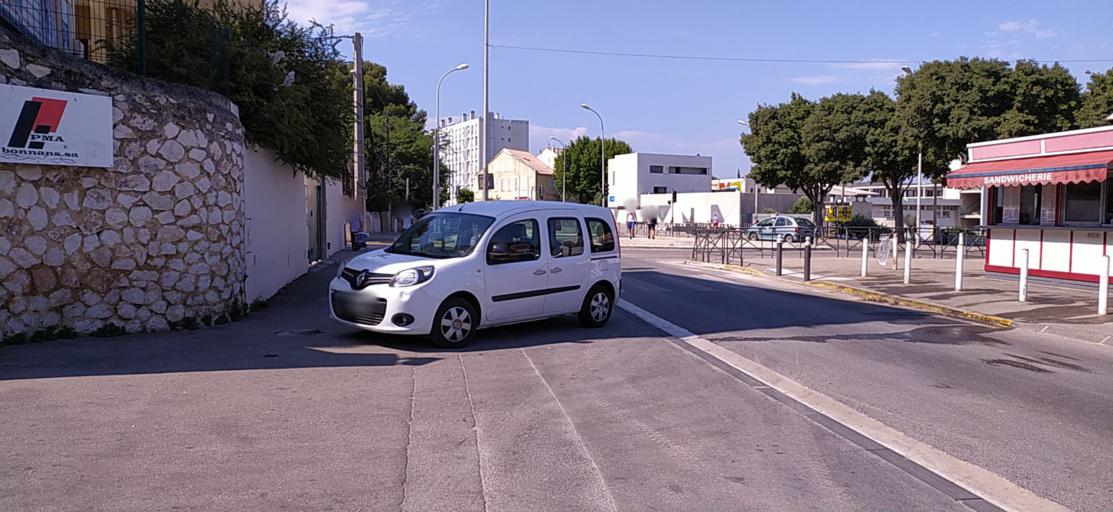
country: FR
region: Provence-Alpes-Cote d'Azur
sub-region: Departement des Bouches-du-Rhone
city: Marseille 14
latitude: 43.3472
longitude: 5.3555
